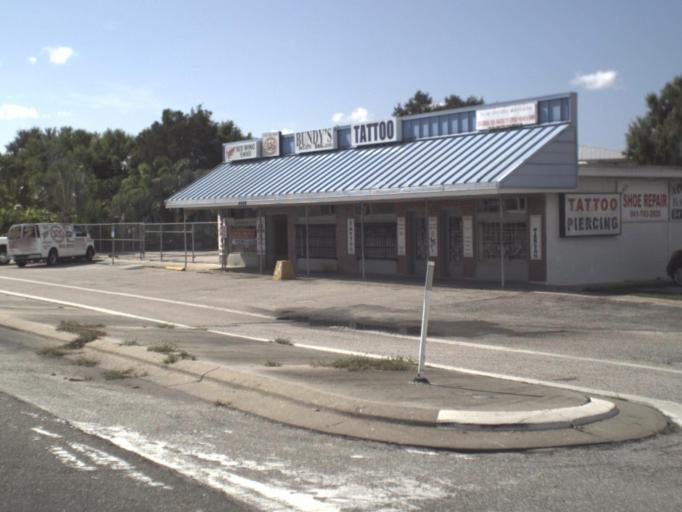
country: US
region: Florida
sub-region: Charlotte County
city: Charlotte Harbor
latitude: 26.9627
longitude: -82.0722
